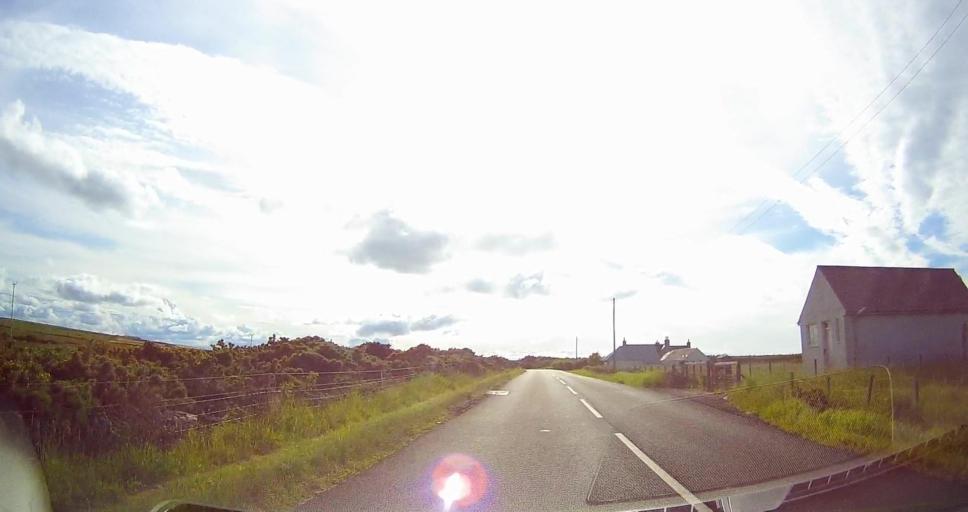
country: GB
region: Scotland
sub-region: Highland
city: Thurso
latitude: 58.6293
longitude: -3.3102
